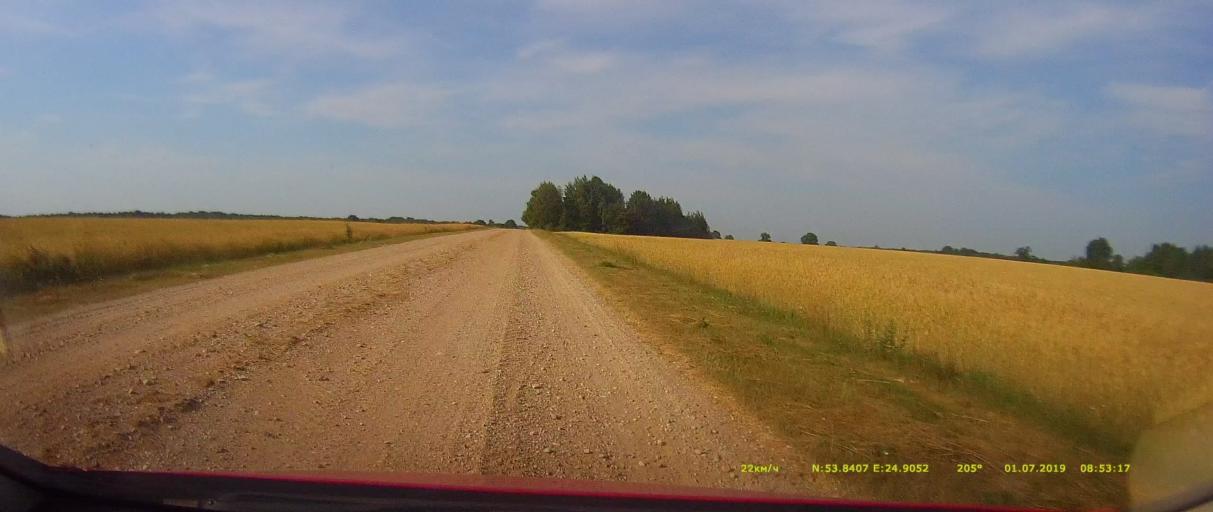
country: BY
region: Grodnenskaya
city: Shchuchin
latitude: 53.8409
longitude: 24.9053
